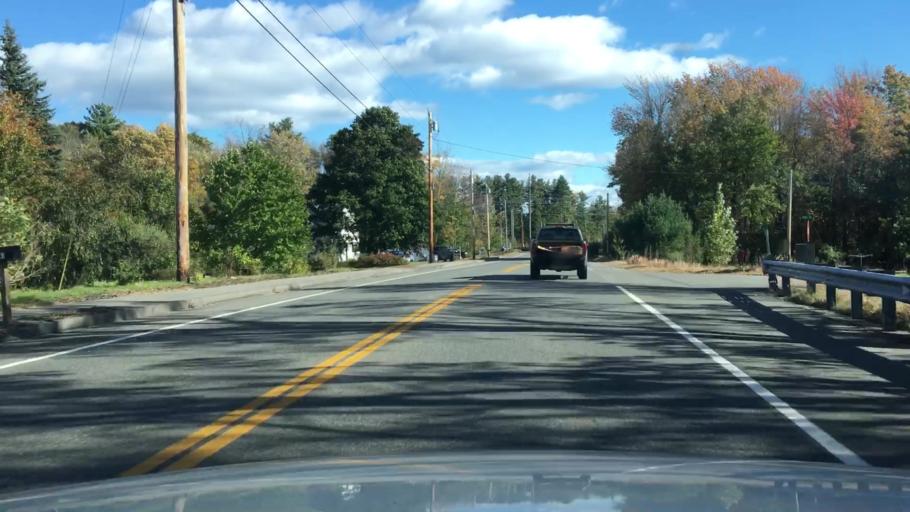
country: US
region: Maine
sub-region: York County
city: Wells Beach Station
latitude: 43.3549
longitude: -70.6532
